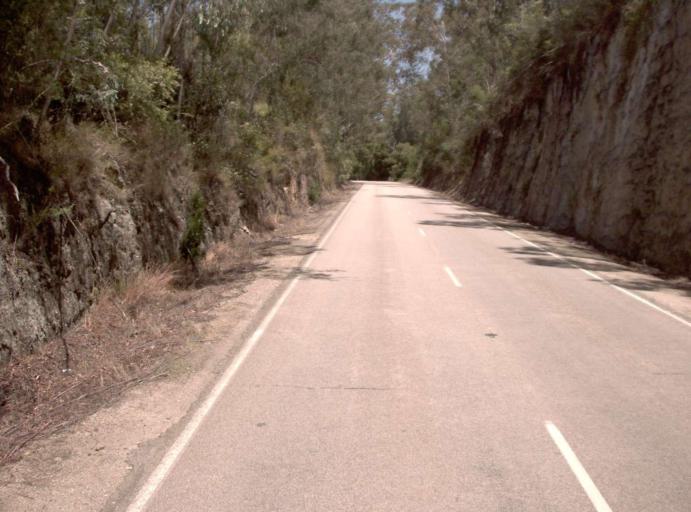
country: AU
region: Victoria
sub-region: East Gippsland
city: Lakes Entrance
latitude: -37.6646
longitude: 147.8731
